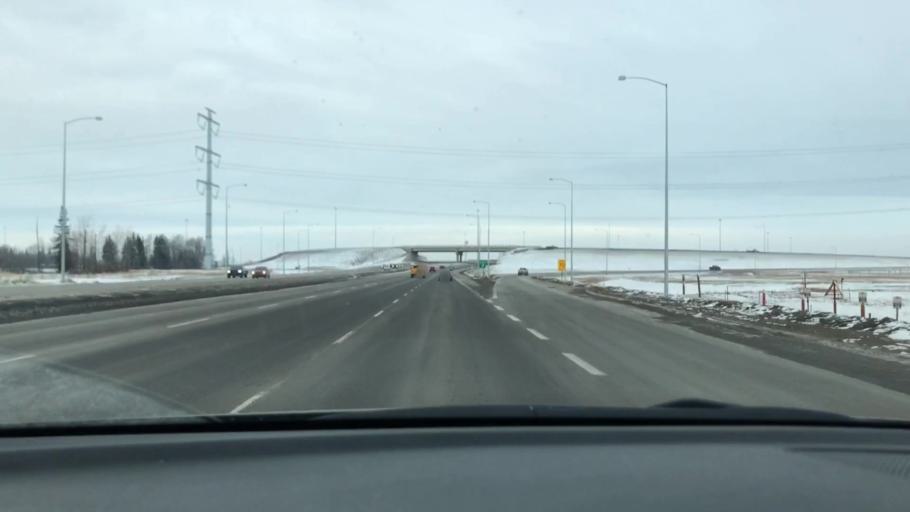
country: CA
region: Alberta
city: Sherwood Park
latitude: 53.5122
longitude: -113.3328
